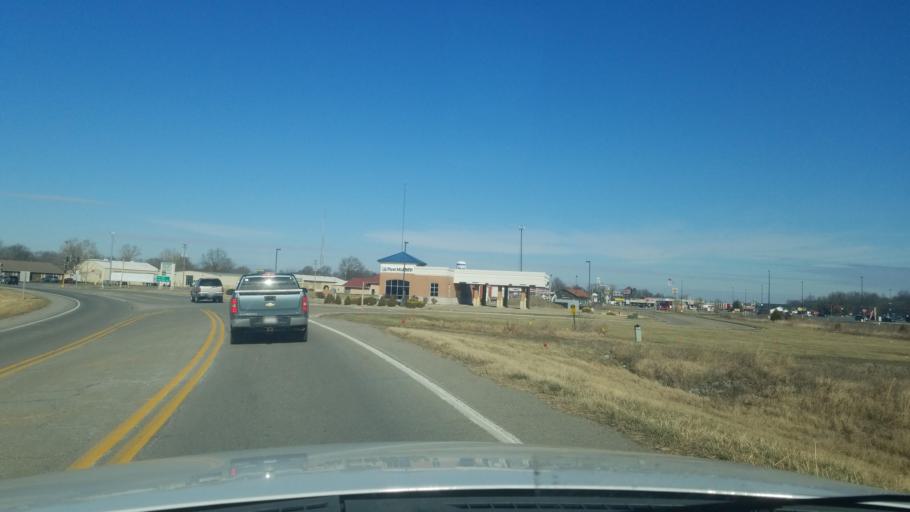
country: US
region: Illinois
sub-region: Saline County
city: Harrisburg
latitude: 37.7254
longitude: -88.5359
